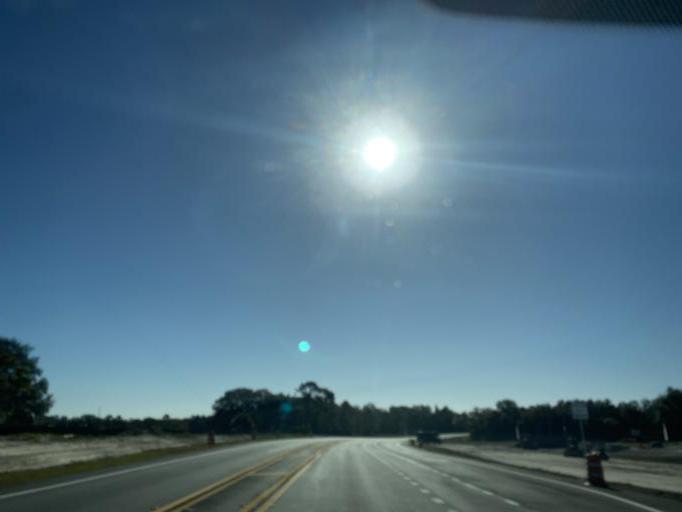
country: US
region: Florida
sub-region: Lake County
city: Mount Plymouth
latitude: 28.8325
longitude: -81.5230
